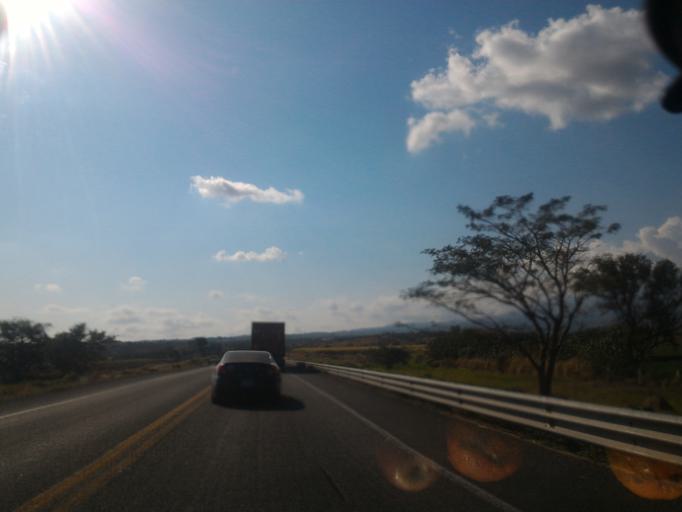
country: MX
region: Jalisco
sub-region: Tonila
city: San Marcos
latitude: 19.4346
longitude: -103.4860
